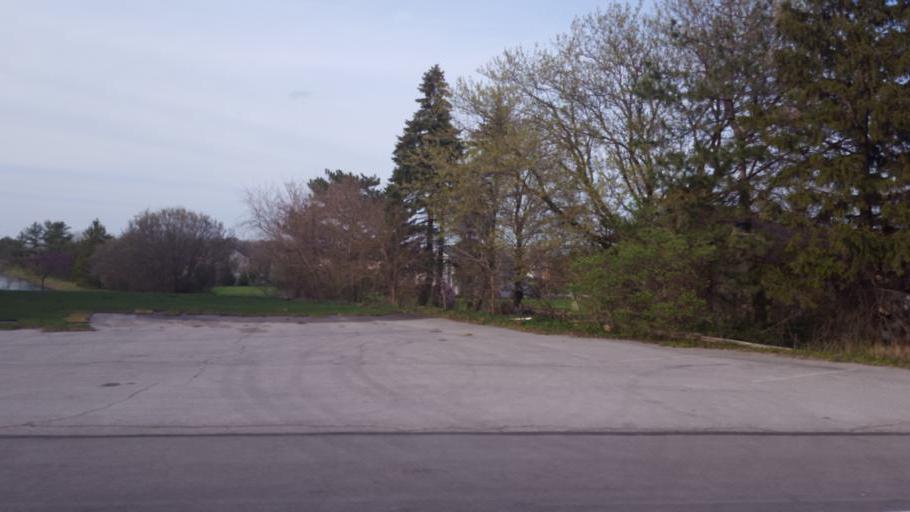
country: US
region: Ohio
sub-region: Erie County
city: Huron
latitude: 41.4123
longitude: -82.6141
